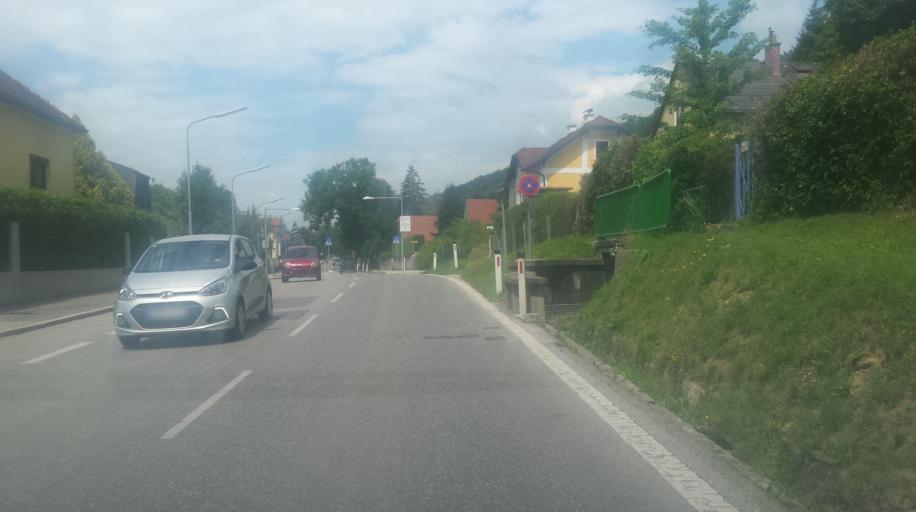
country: AT
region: Lower Austria
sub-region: Politischer Bezirk Wien-Umgebung
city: Purkersdorf
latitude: 48.2275
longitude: 16.2059
